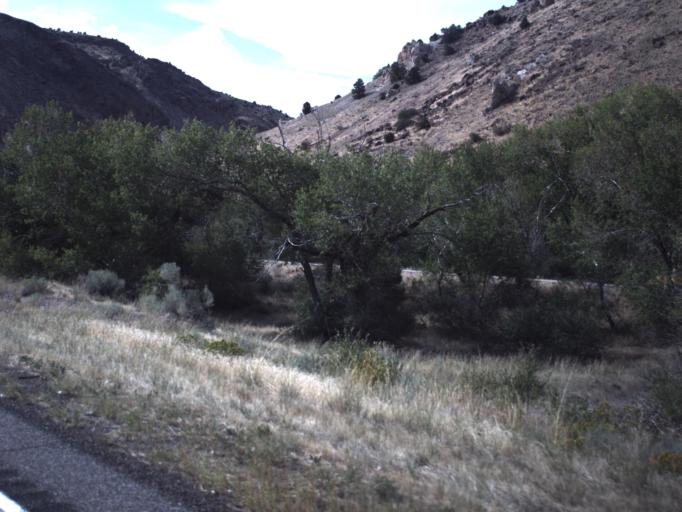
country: US
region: Utah
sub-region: Sevier County
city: Monroe
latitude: 38.5711
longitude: -112.2547
